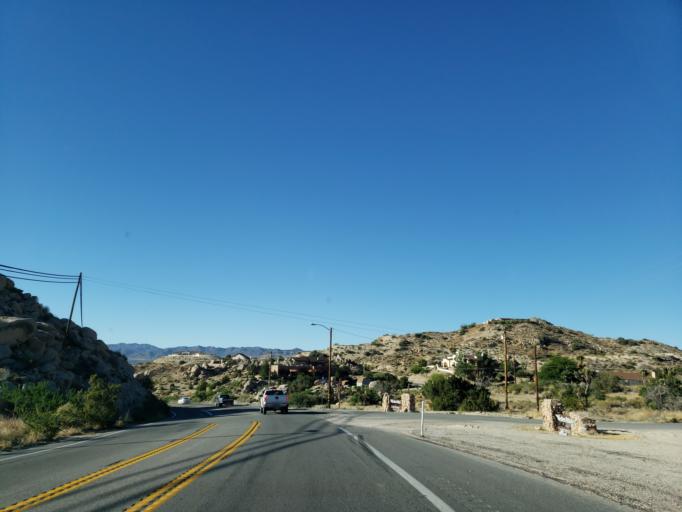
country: US
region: California
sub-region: San Bernardino County
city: Yucca Valley
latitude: 34.1481
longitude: -116.4189
